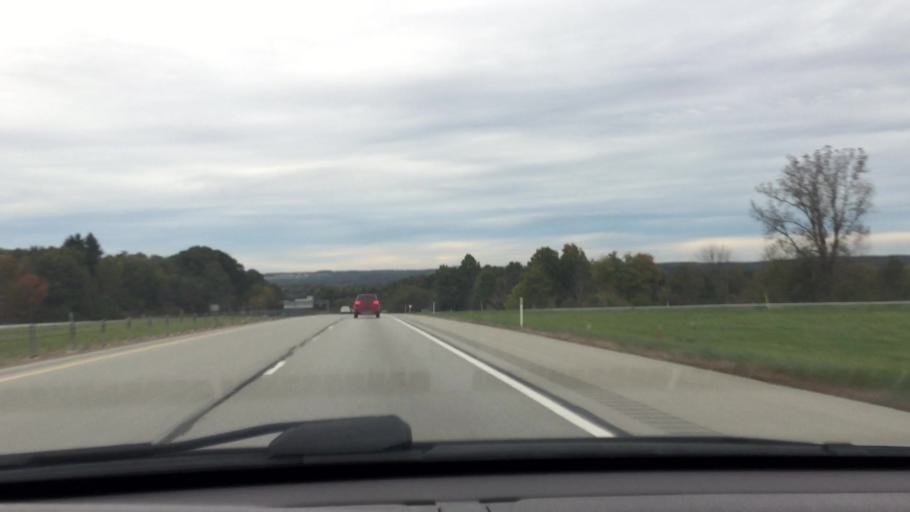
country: US
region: Pennsylvania
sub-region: Lawrence County
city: Oakwood
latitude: 41.0130
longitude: -80.3904
